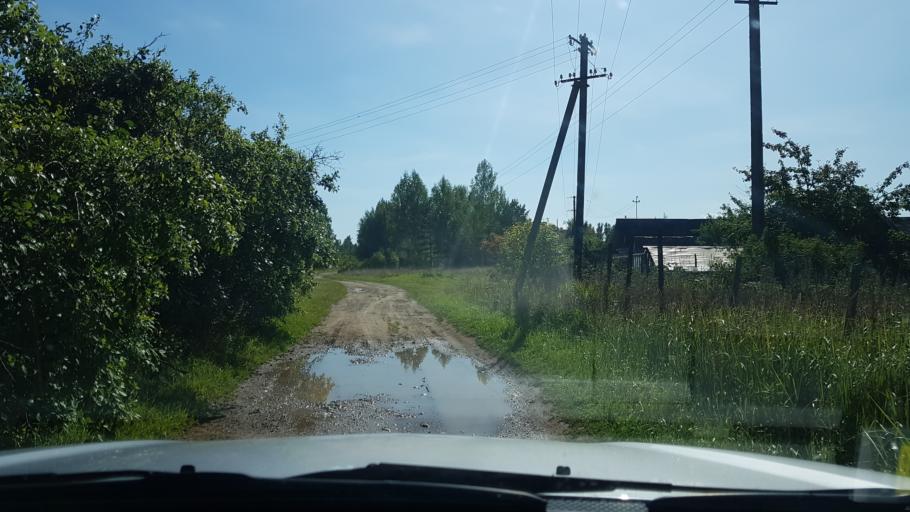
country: EE
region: Ida-Virumaa
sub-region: Sillamaee linn
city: Sillamae
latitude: 59.3246
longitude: 27.7764
